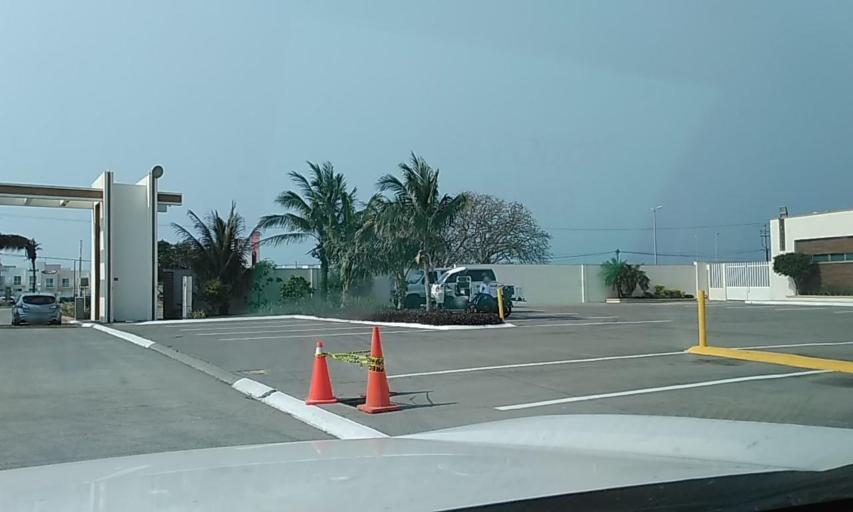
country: MX
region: Veracruz
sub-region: Alvarado
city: Playa de la Libertad
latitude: 19.0557
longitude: -96.0614
